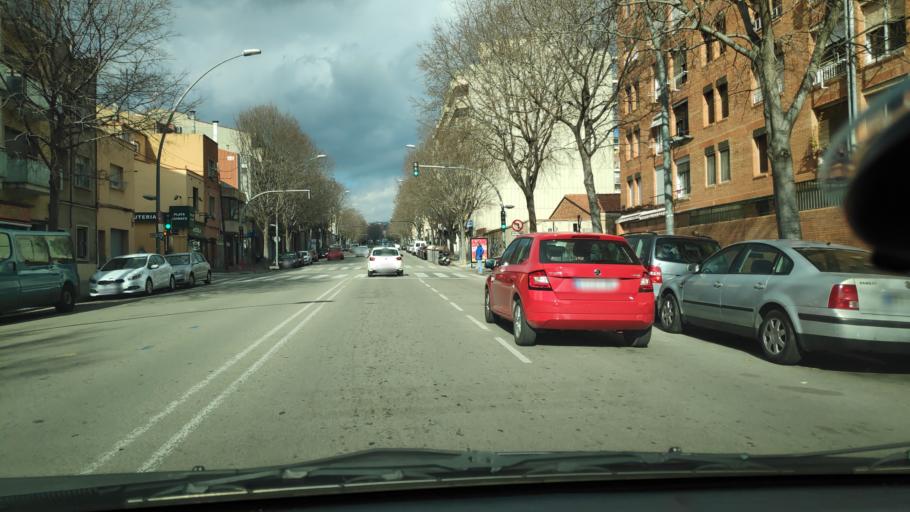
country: ES
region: Catalonia
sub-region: Provincia de Barcelona
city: Terrassa
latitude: 41.5586
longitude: 1.9998
